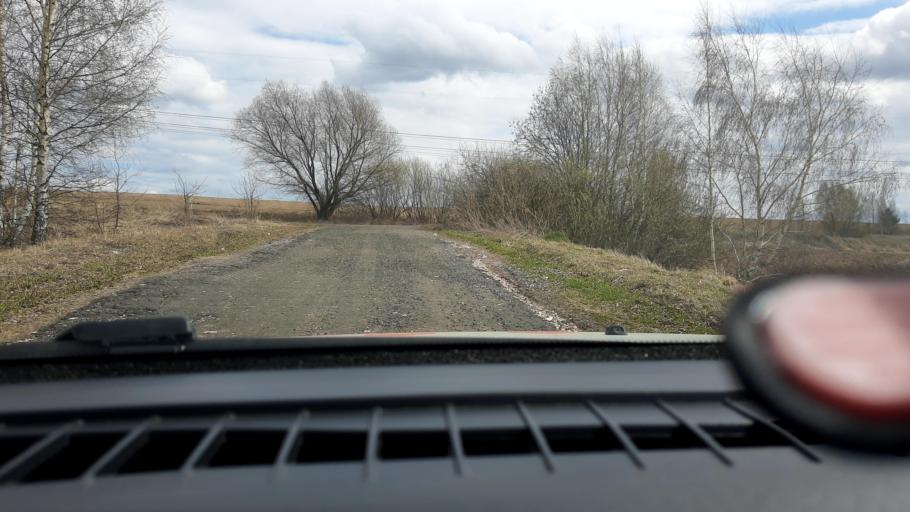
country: RU
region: Nizjnij Novgorod
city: Babino
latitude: 56.1710
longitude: 43.6760
